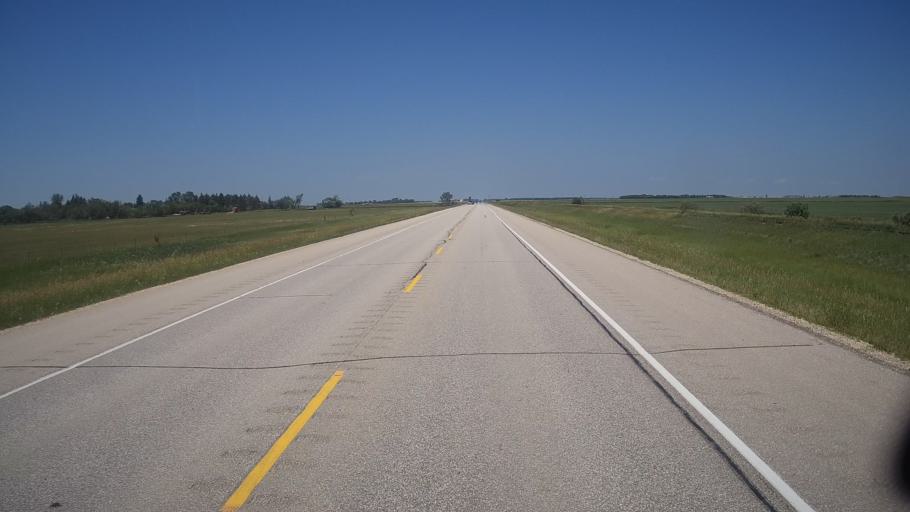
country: CA
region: Manitoba
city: Stonewall
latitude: 50.0167
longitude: -97.3696
